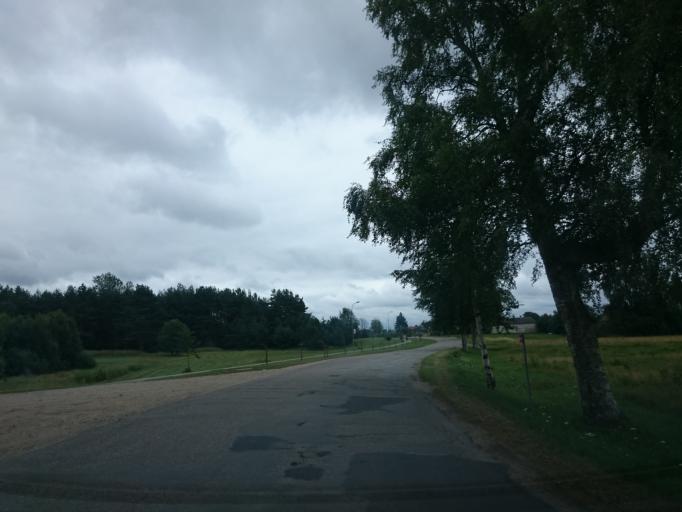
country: LV
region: Pavilostas
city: Pavilosta
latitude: 56.8867
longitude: 21.1911
